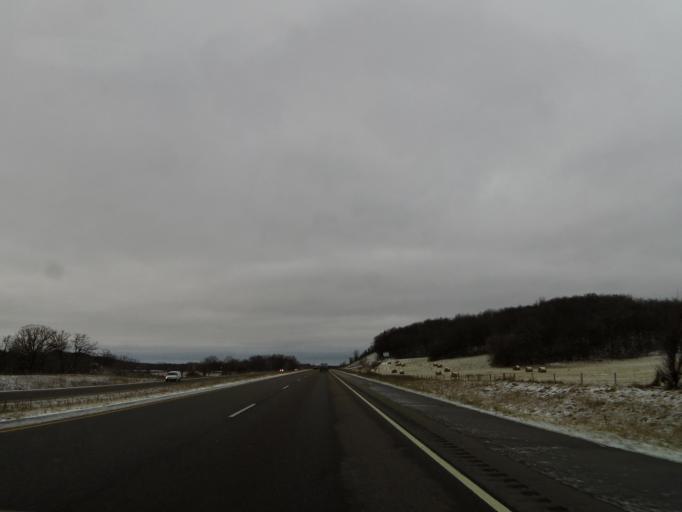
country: US
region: Wisconsin
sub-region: Eau Claire County
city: Fall Creek
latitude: 44.6851
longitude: -91.3308
